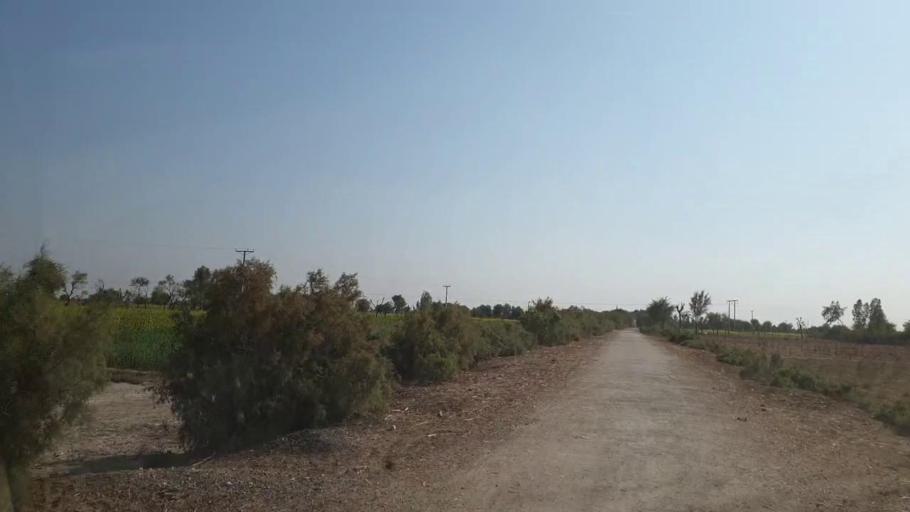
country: PK
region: Sindh
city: Mirpur Khas
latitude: 25.7220
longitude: 69.1553
